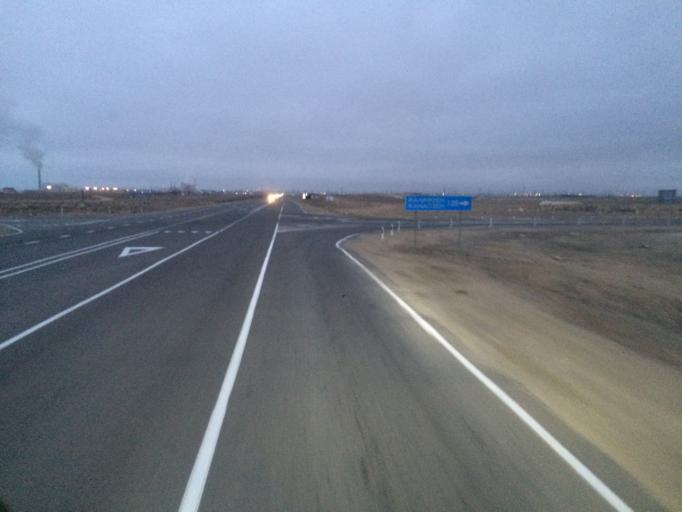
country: KZ
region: Mangghystau
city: Omirzaq
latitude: 43.5862
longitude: 51.3272
